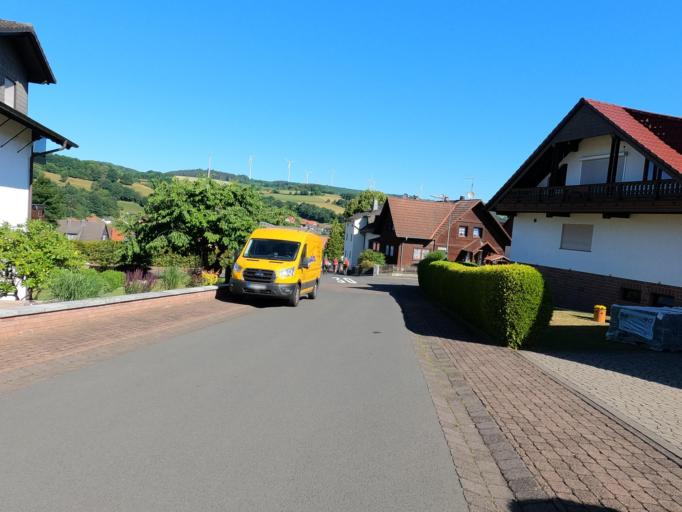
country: DE
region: Bavaria
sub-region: Regierungsbezirk Unterfranken
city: Zeitlofs
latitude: 50.3104
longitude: 9.6710
